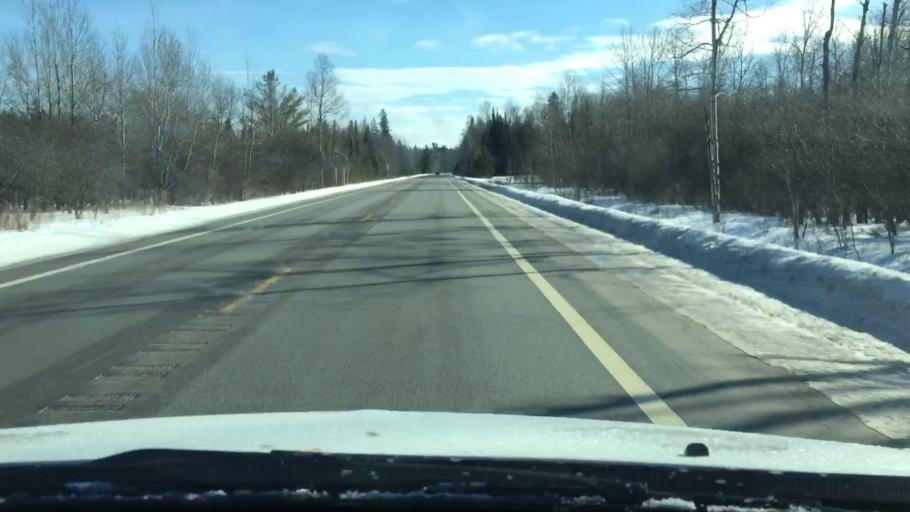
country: US
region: Michigan
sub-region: Charlevoix County
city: East Jordan
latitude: 45.0599
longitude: -85.0774
